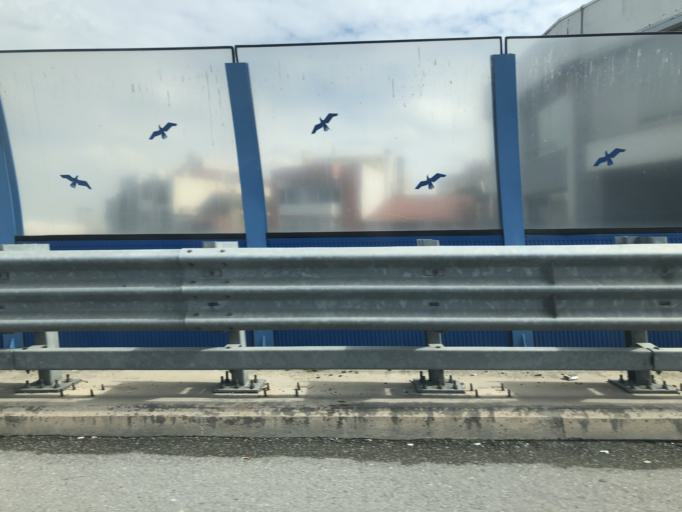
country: TR
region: Izmir
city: Karabaglar
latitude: 38.3953
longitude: 27.0633
